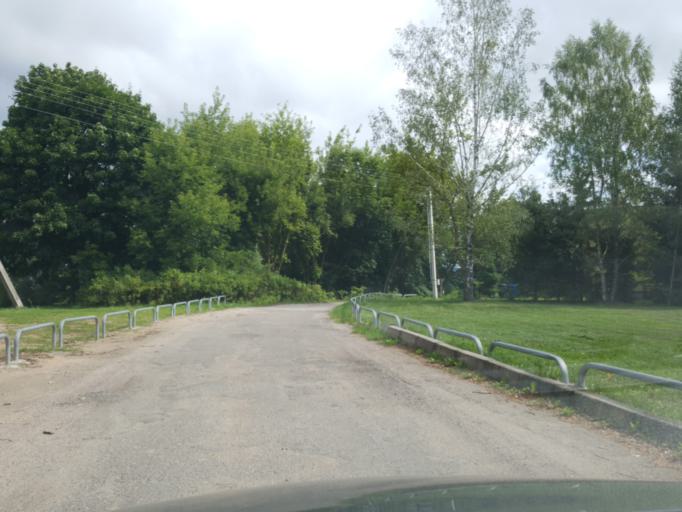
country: LT
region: Alytaus apskritis
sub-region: Alytus
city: Alytus
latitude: 54.4011
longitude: 24.0377
